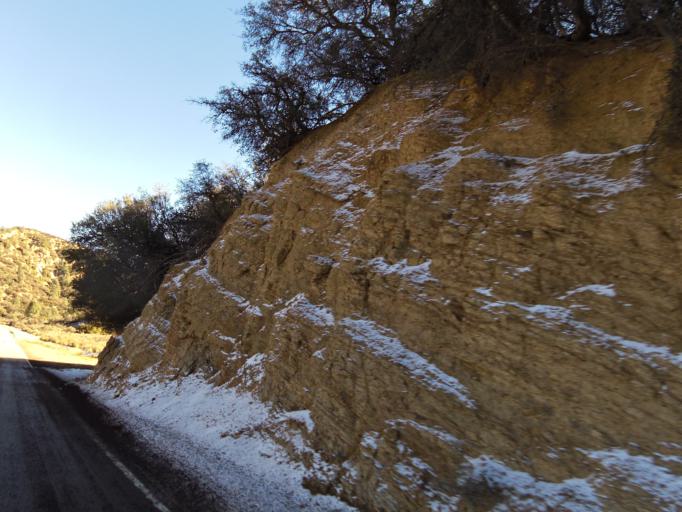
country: US
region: California
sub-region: Ventura County
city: Meiners Oaks
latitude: 34.6784
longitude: -119.3629
